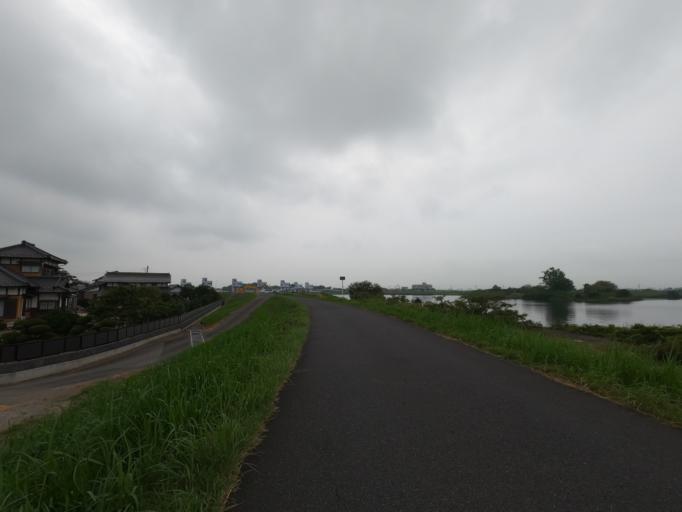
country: JP
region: Ibaraki
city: Moriya
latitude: 35.9323
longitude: 140.0463
